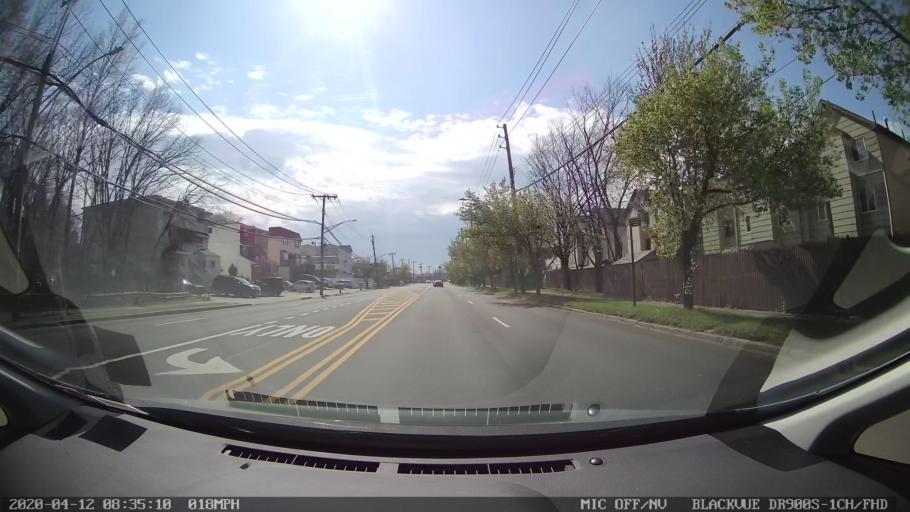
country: US
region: New York
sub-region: Richmond County
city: Bloomfield
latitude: 40.6081
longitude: -74.1583
